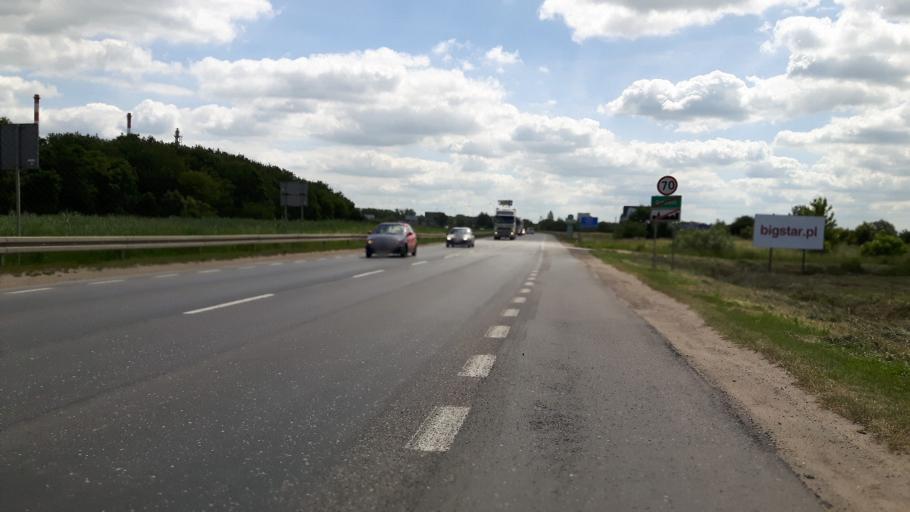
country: PL
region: Pomeranian Voivodeship
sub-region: Gdansk
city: Gdansk
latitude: 54.3417
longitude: 18.7269
